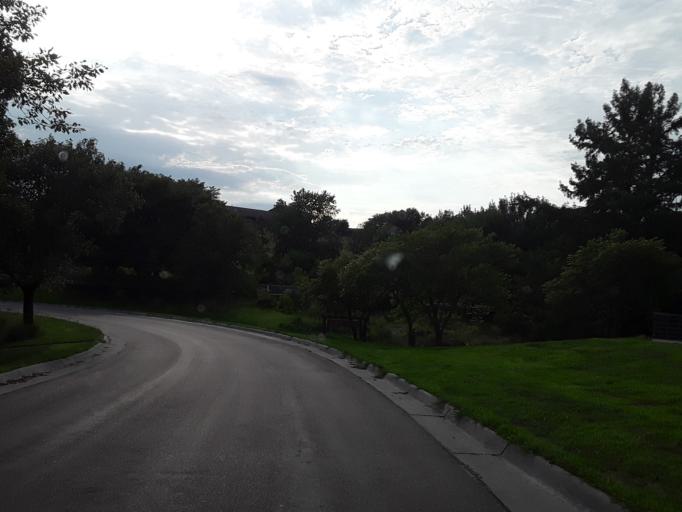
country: US
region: Nebraska
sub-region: Saunders County
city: Ashland
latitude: 41.0232
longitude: -96.3118
